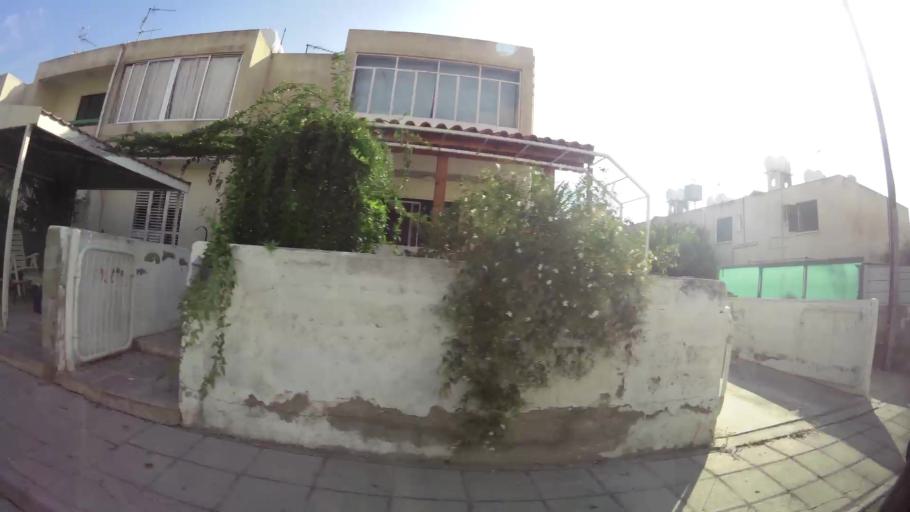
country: CY
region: Lefkosia
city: Nicosia
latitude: 35.1779
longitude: 33.3388
